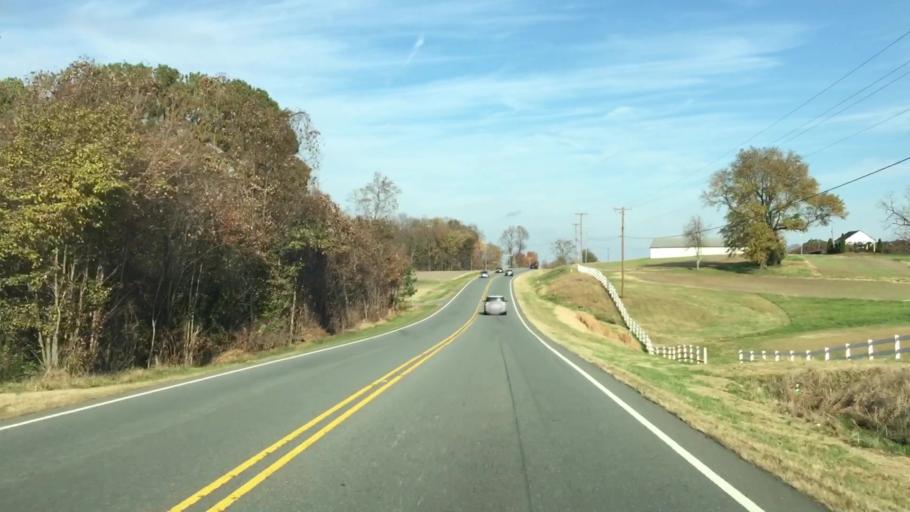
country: US
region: North Carolina
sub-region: Forsyth County
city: Walkertown
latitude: 36.1886
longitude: -80.1082
